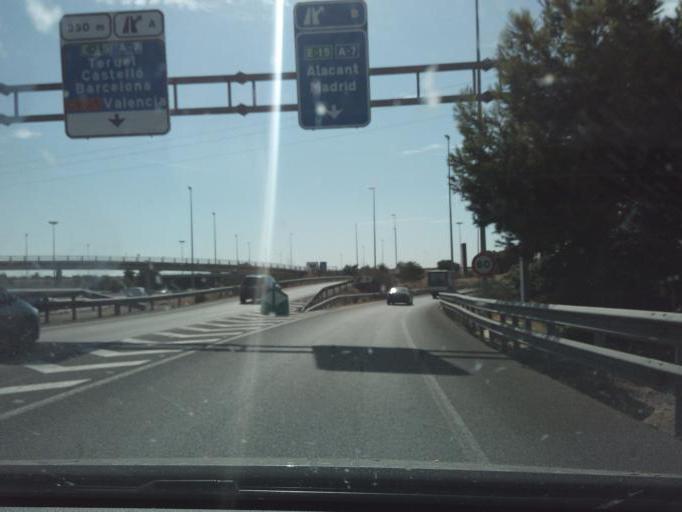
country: ES
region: Valencia
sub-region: Provincia de Valencia
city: Godella
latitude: 39.5413
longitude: -0.4556
